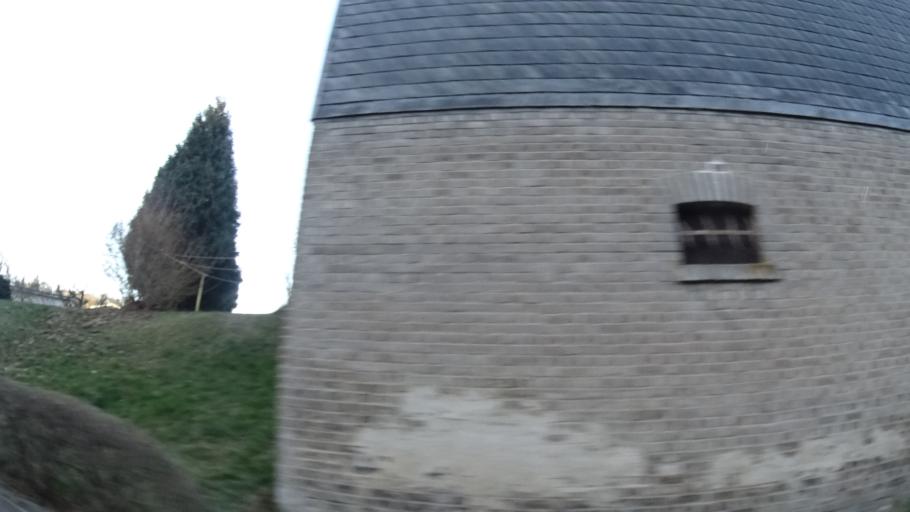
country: DE
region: Thuringia
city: Grafenthal
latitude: 50.5340
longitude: 11.3015
